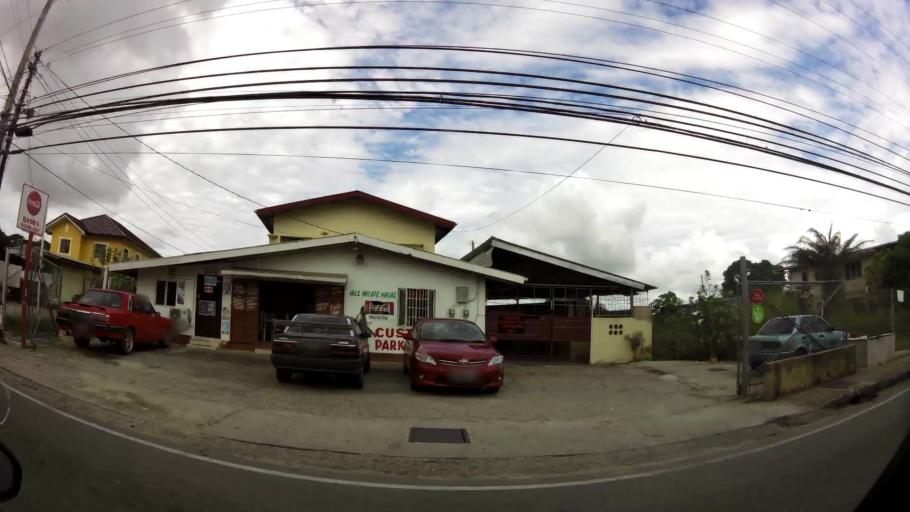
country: TT
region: Chaguanas
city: Chaguanas
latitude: 10.4731
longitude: -61.4132
